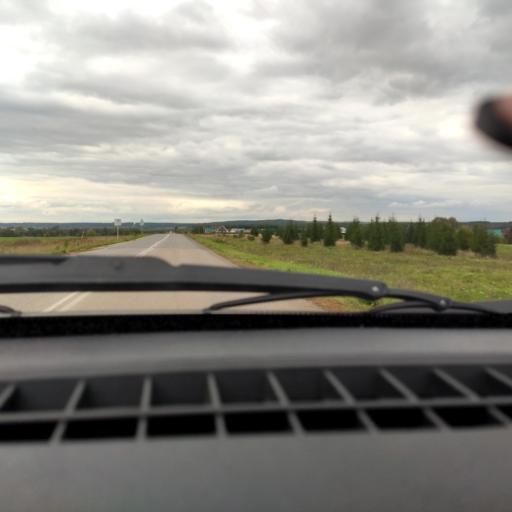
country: RU
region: Bashkortostan
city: Iglino
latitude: 54.7093
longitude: 56.4000
